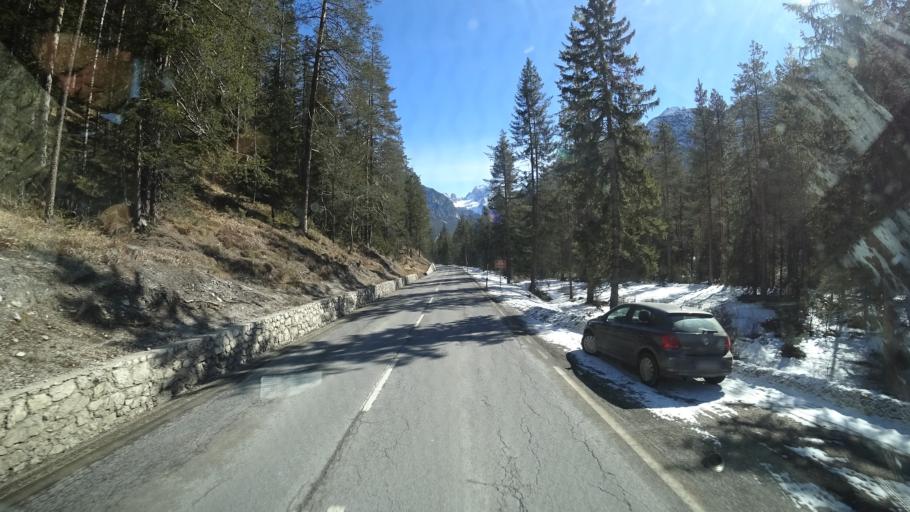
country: IT
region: Veneto
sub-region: Provincia di Belluno
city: Cortina d'Ampezzo
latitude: 46.6237
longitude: 12.1986
